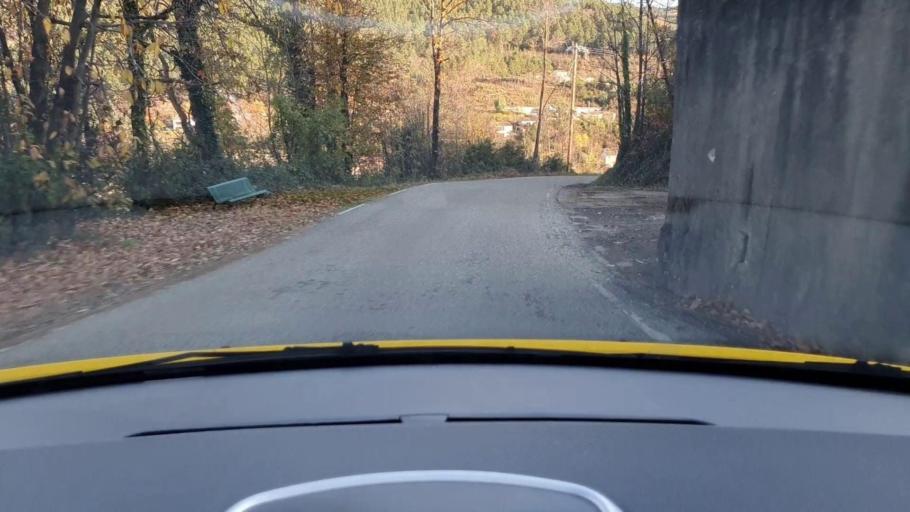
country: FR
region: Languedoc-Roussillon
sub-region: Departement du Gard
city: Branoux-les-Taillades
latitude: 44.2292
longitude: 4.0019
